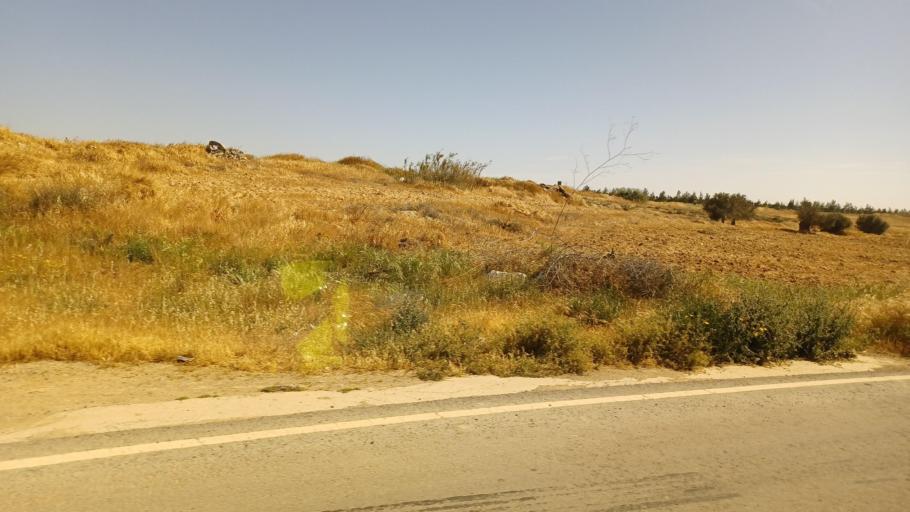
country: CY
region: Lefkosia
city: Kokkinotrimithia
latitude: 35.1576
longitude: 33.1831
